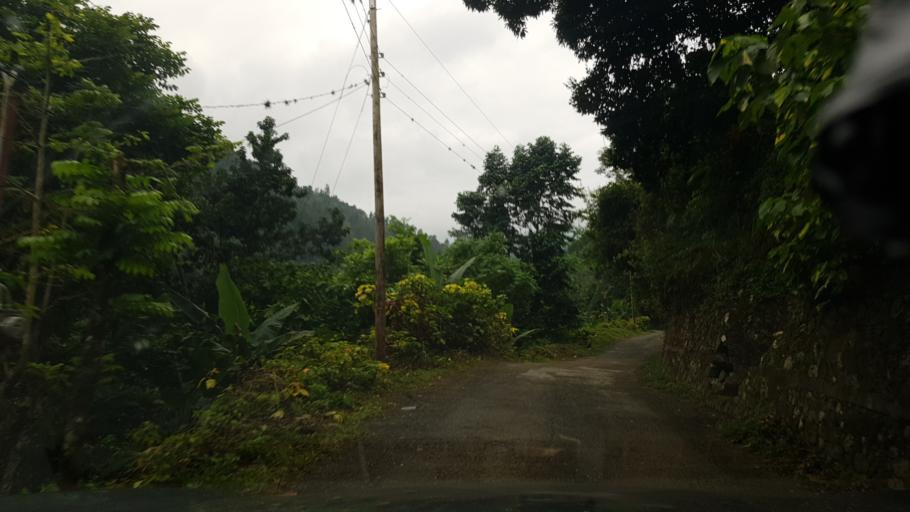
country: JM
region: Saint Andrew
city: Stony Hill
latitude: 18.1264
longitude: -76.7159
